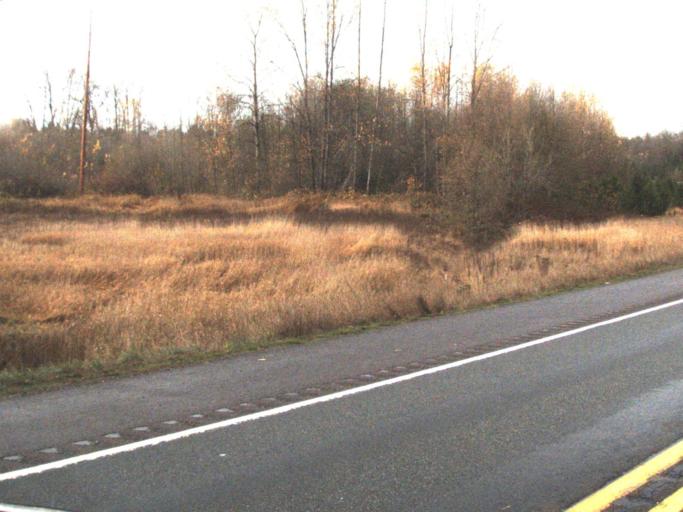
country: US
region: Washington
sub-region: Snohomish County
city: Snohomish
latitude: 47.9385
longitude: -122.0700
